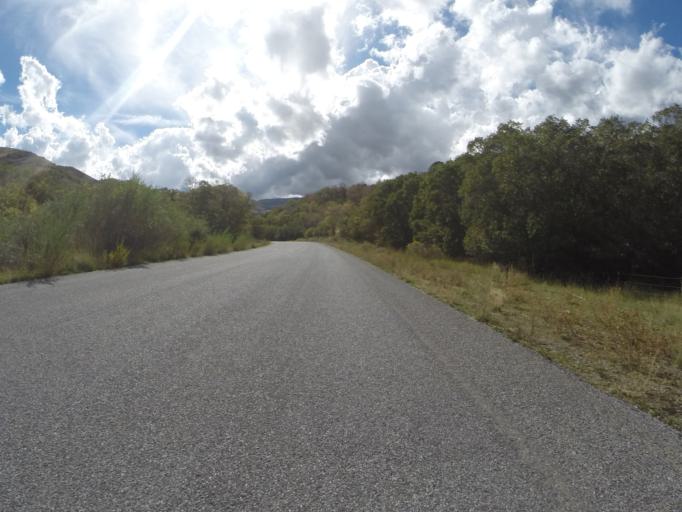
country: US
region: Utah
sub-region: Salt Lake County
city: Herriman
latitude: 40.4946
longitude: -112.1158
